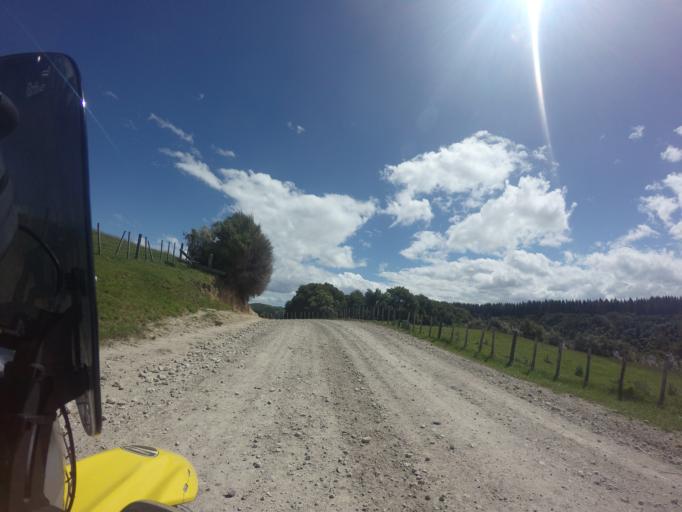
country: NZ
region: Hawke's Bay
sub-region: Wairoa District
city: Wairoa
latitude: -38.9697
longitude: 177.7031
